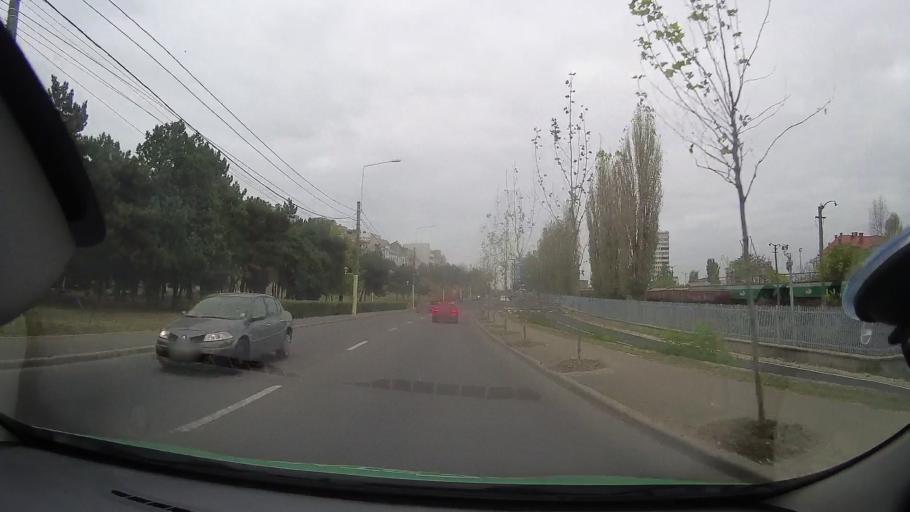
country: RO
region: Constanta
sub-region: Municipiul Constanta
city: Constanta
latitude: 44.1730
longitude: 28.6573
